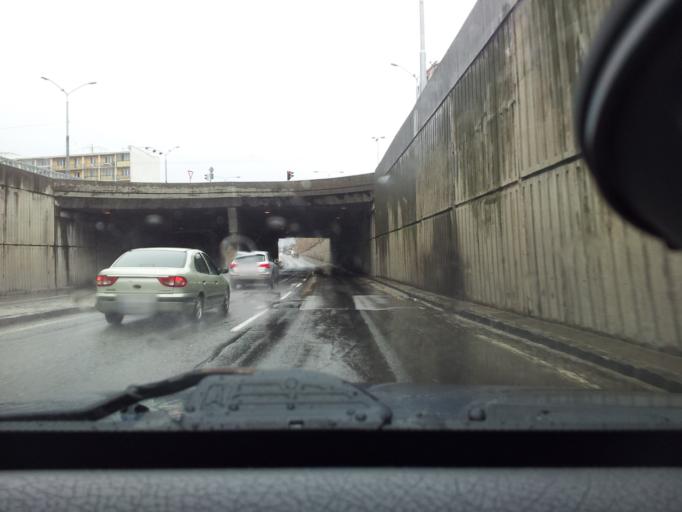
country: SK
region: Bratislavsky
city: Bratislava
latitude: 48.1482
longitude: 17.1501
